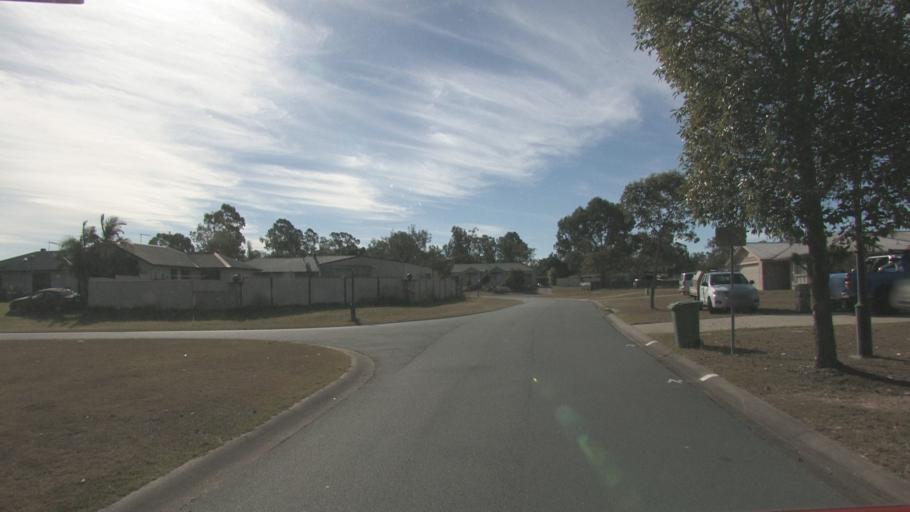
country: AU
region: Queensland
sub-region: Logan
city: North Maclean
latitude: -27.8116
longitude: 152.9531
